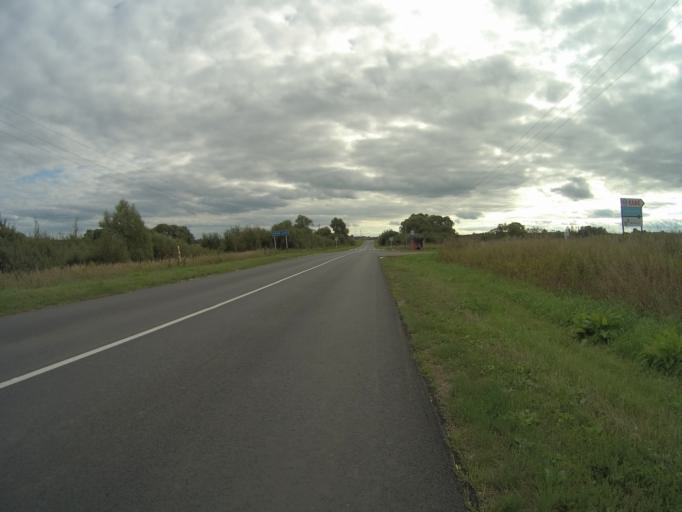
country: RU
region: Vladimir
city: Bogolyubovo
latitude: 56.2848
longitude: 40.5332
